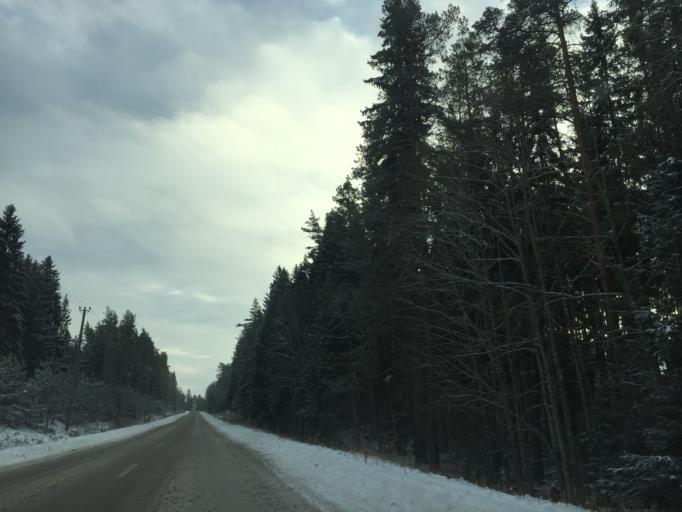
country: LV
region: Amatas Novads
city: Drabesi
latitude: 57.2178
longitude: 25.2927
